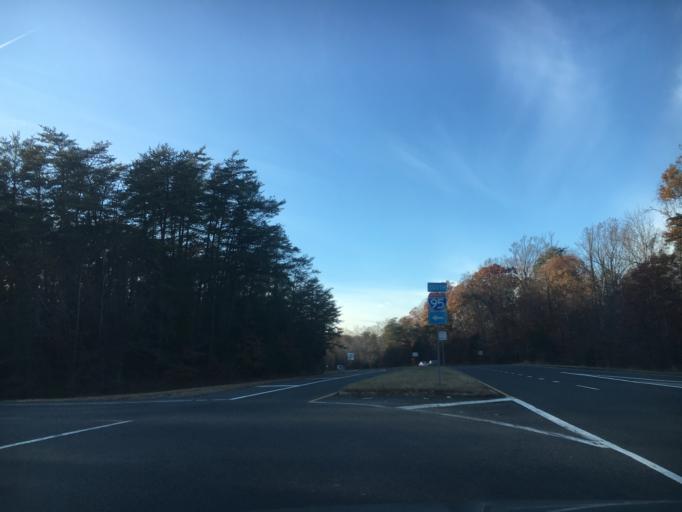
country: US
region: Virginia
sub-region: Prince William County
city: Triangle
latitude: 38.5508
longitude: -77.3457
